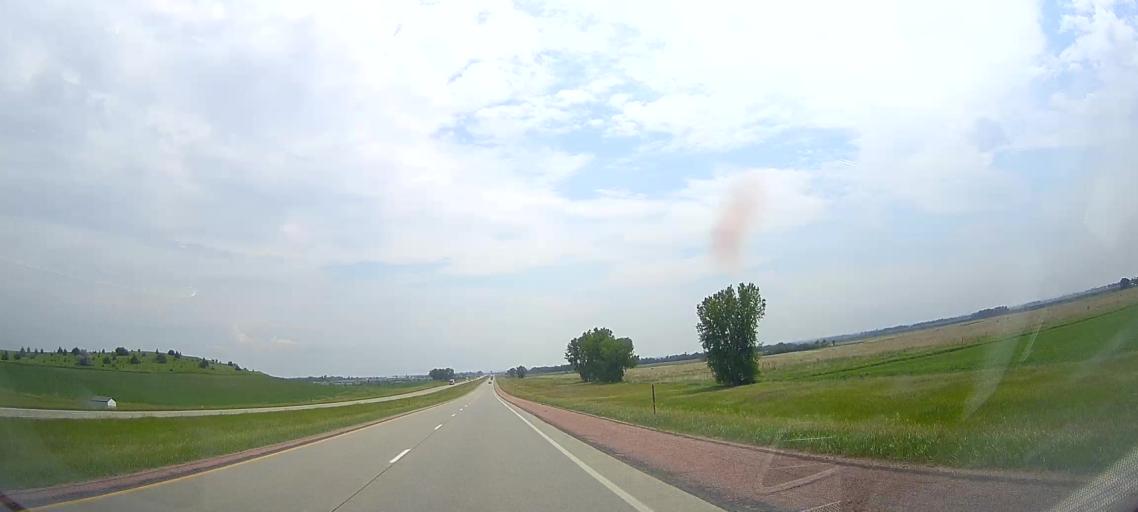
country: US
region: South Dakota
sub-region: Clay County
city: Vermillion
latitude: 42.8958
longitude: -96.7952
